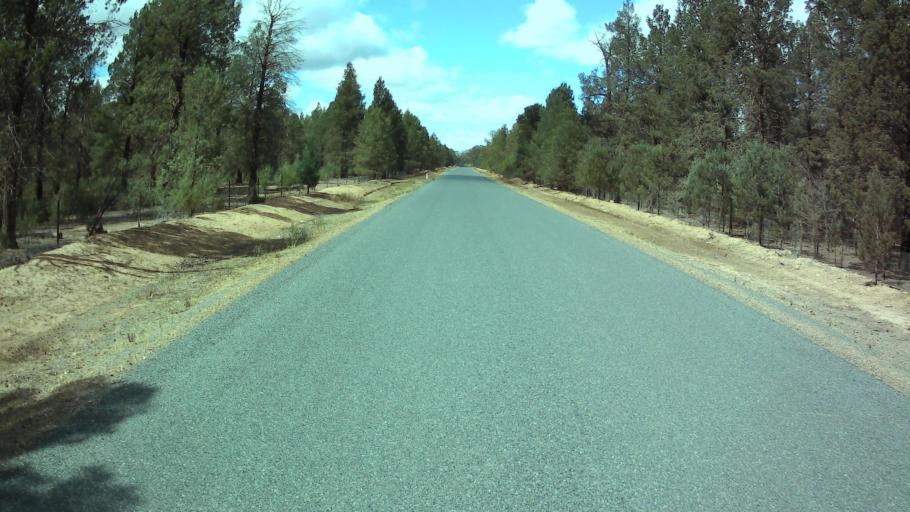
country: AU
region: New South Wales
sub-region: Weddin
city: Grenfell
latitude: -33.8996
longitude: 147.9210
